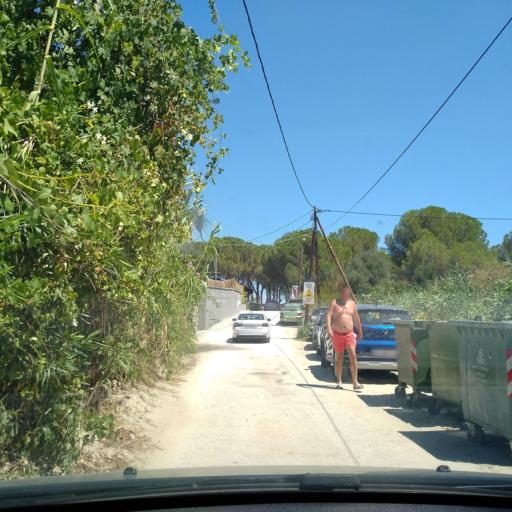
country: GR
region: Central Macedonia
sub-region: Nomos Chalkidikis
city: Neos Marmaras
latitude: 40.1915
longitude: 23.8077
